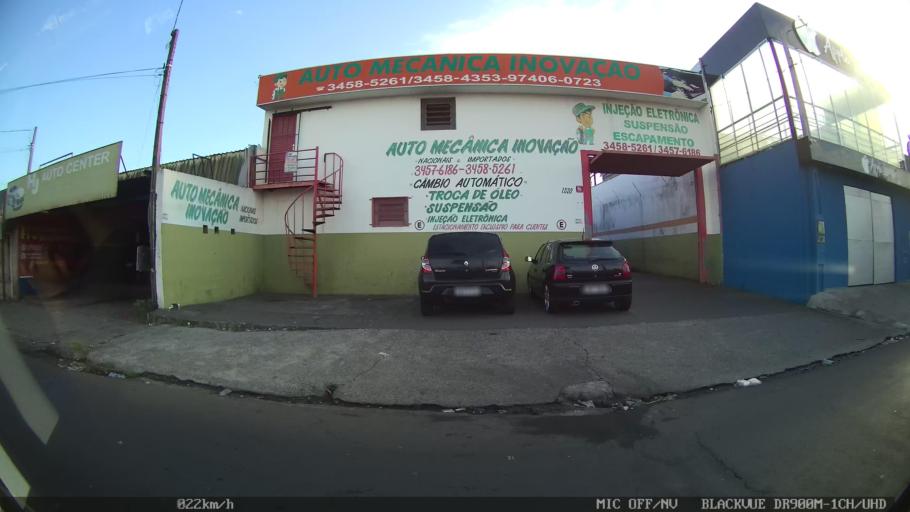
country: BR
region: Sao Paulo
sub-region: Americana
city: Americana
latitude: -22.7474
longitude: -47.3691
